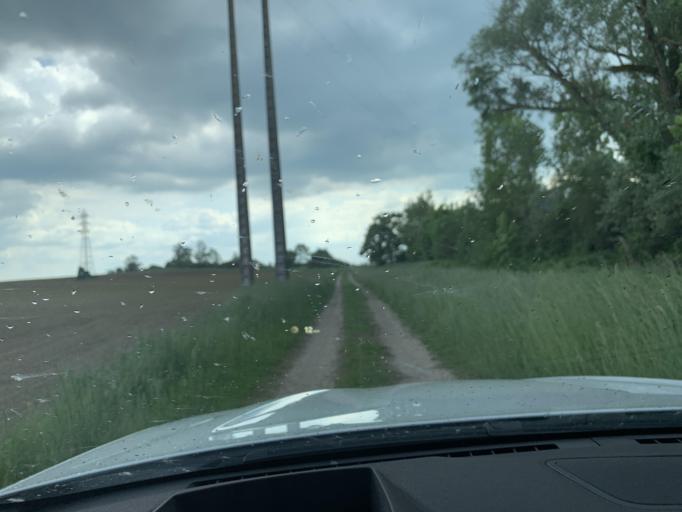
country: FR
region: Bourgogne
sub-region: Departement de Saone-et-Loire
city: Saint-Remy
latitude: 46.7508
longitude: 4.8336
